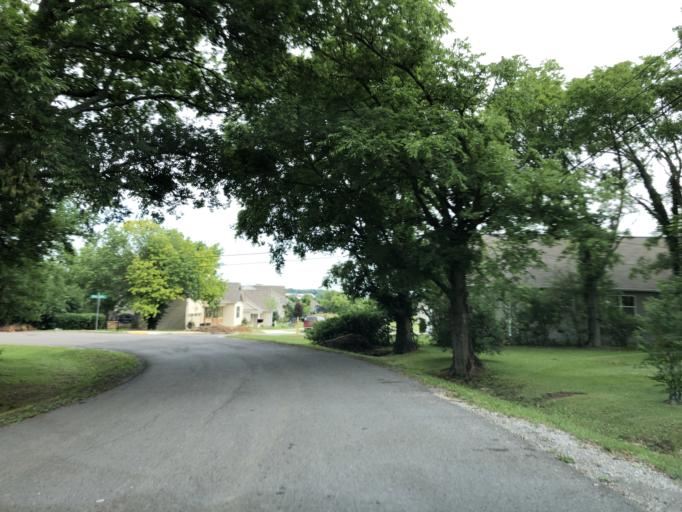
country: US
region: Tennessee
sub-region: Davidson County
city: Goodlettsville
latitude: 36.2793
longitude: -86.6991
